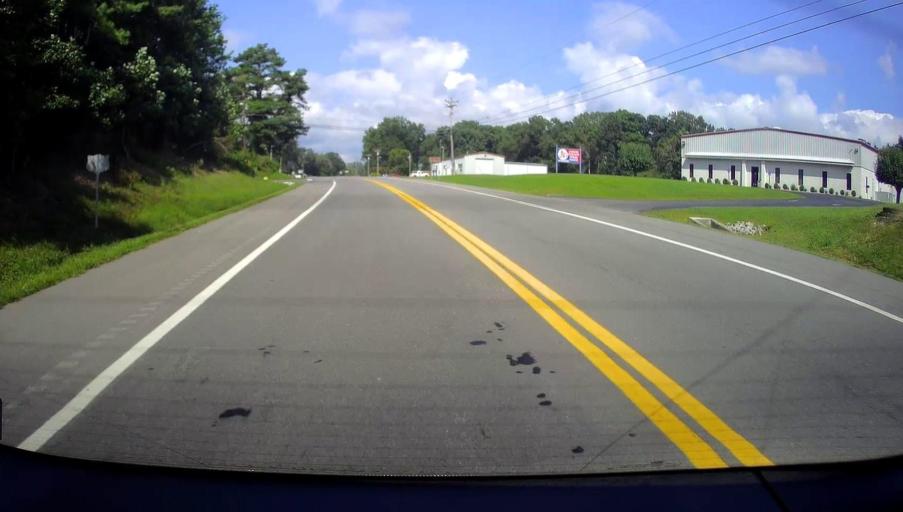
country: US
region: Tennessee
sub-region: Coffee County
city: Manchester
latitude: 35.4980
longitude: -86.1069
